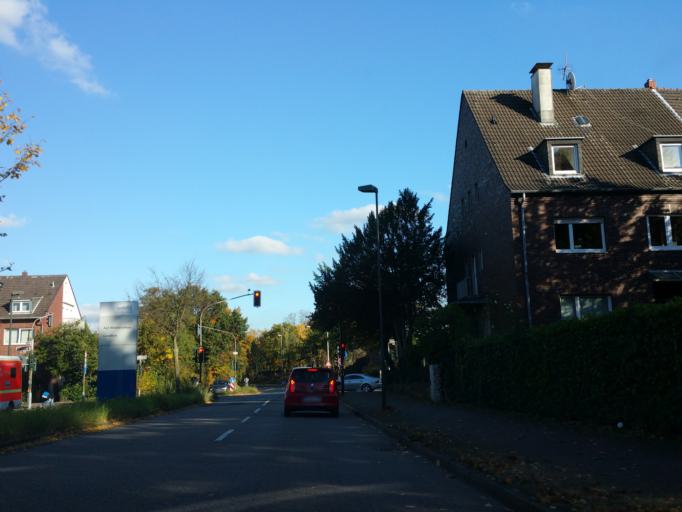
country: DE
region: North Rhine-Westphalia
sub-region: Regierungsbezirk Dusseldorf
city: Dusseldorf
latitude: 51.1923
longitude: 6.7963
